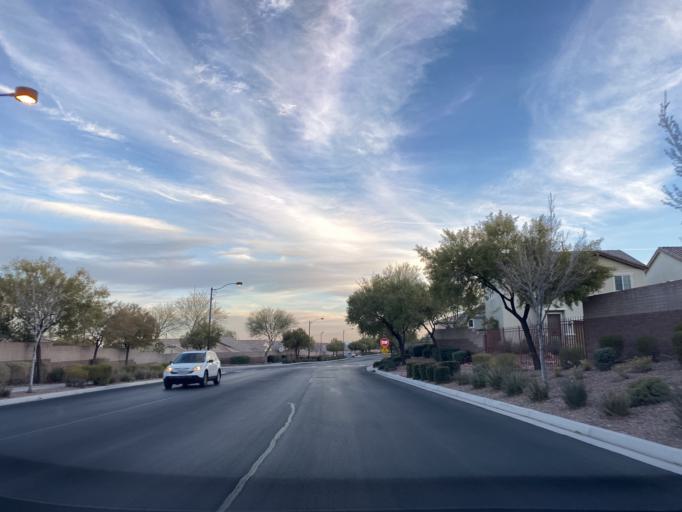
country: US
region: Nevada
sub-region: Clark County
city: Summerlin South
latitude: 36.3041
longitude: -115.3249
